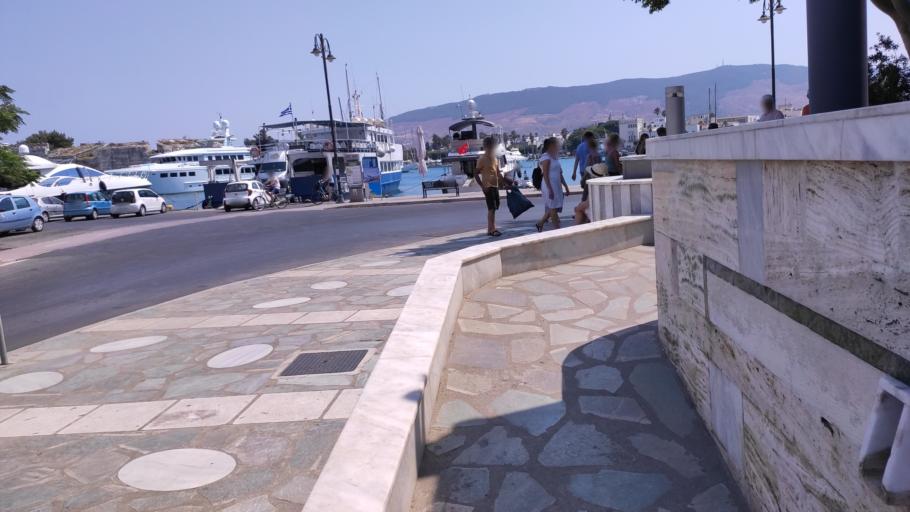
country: GR
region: South Aegean
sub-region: Nomos Dodekanisou
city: Kos
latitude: 36.8974
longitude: 27.2875
